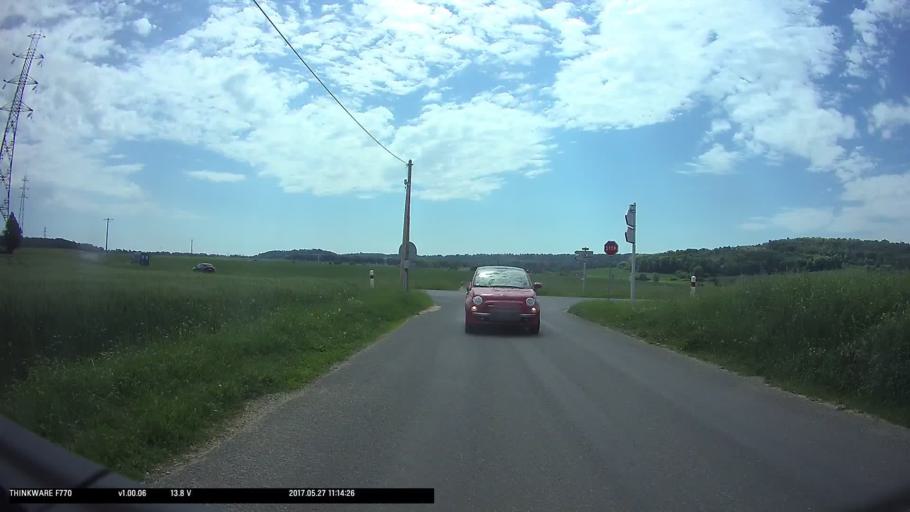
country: FR
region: Picardie
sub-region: Departement de l'Oise
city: Trie-Chateau
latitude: 49.2823
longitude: 1.8445
